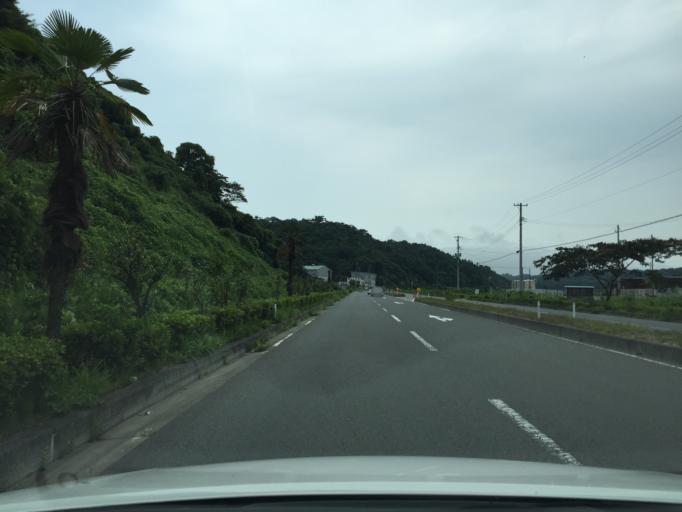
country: JP
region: Fukushima
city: Iwaki
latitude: 36.9658
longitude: 140.9189
